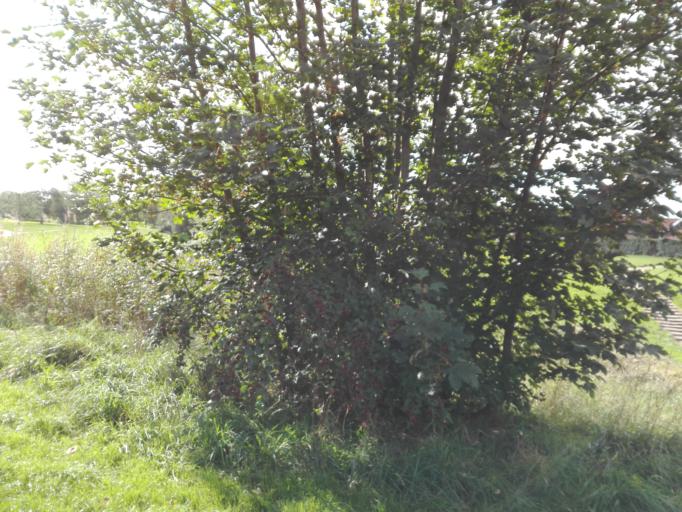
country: DK
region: Central Jutland
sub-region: Arhus Kommune
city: Beder
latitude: 56.0627
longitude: 10.2090
